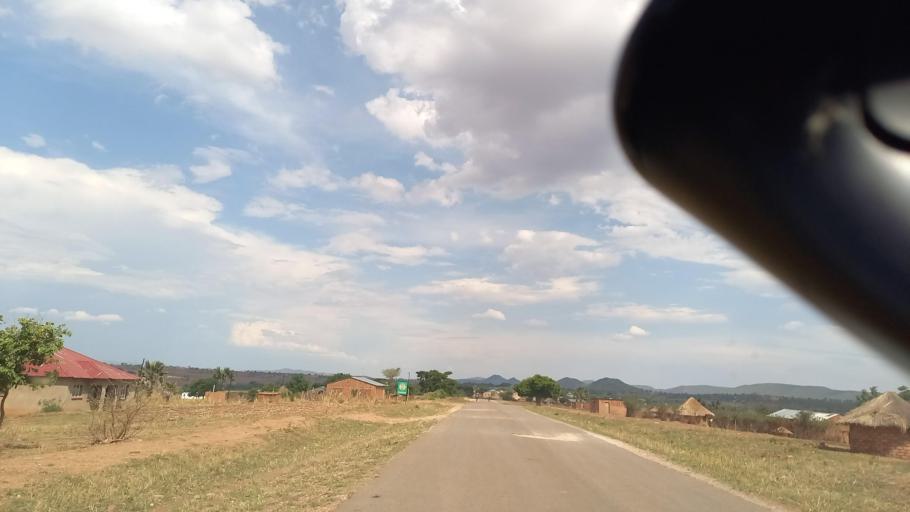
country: ZM
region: Lusaka
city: Kafue
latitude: -16.2176
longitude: 28.1169
